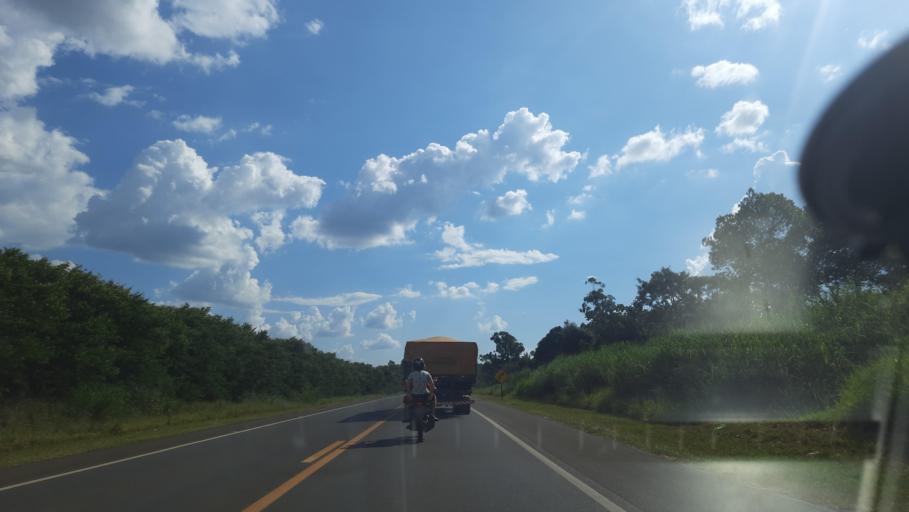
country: BR
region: Sao Paulo
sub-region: Casa Branca
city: Casa Branca
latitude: -21.7537
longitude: -46.9990
